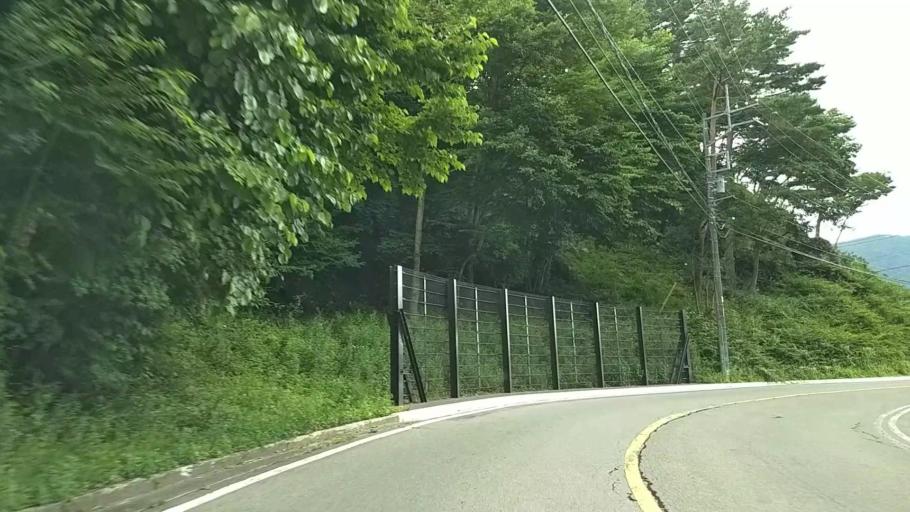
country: JP
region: Yamanashi
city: Fujikawaguchiko
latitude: 35.5022
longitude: 138.6987
